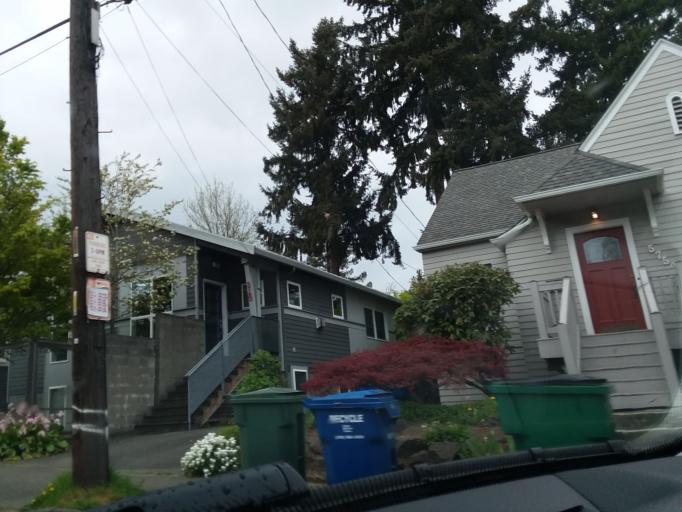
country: US
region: Washington
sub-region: King County
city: Seattle
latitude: 47.6717
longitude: -122.3006
